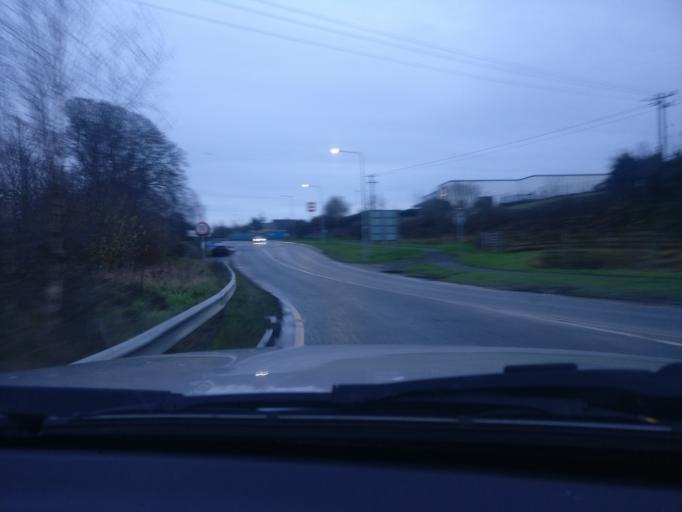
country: IE
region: Leinster
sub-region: An Mhi
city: Kells
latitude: 53.7323
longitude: -6.8912
